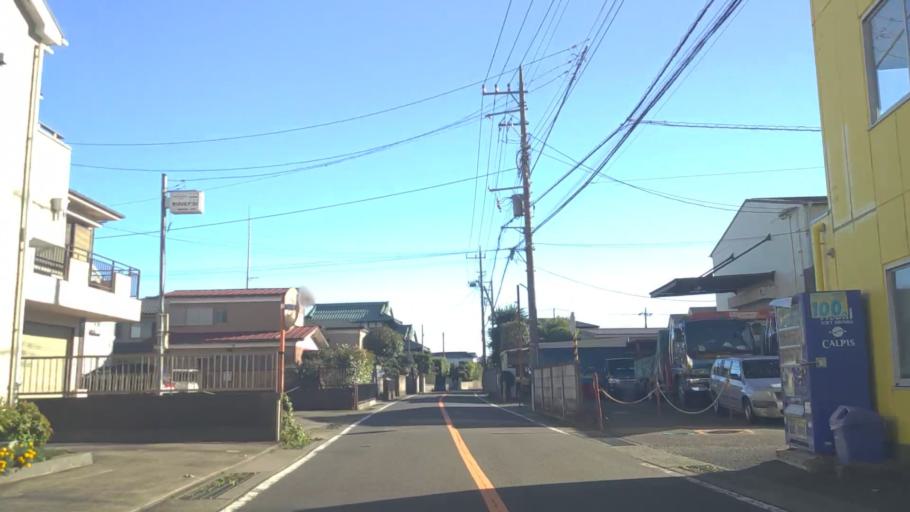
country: JP
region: Kanagawa
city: Atsugi
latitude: 35.4274
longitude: 139.3691
